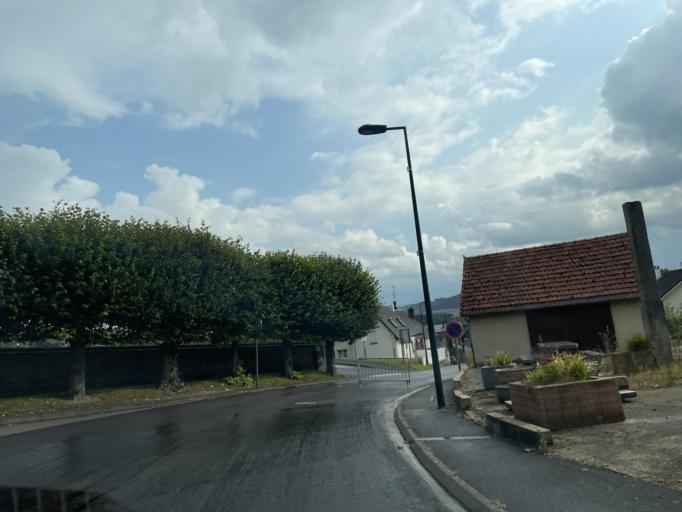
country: FR
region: Haute-Normandie
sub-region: Departement de la Seine-Maritime
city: Envermeu
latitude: 49.8989
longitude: 1.2634
